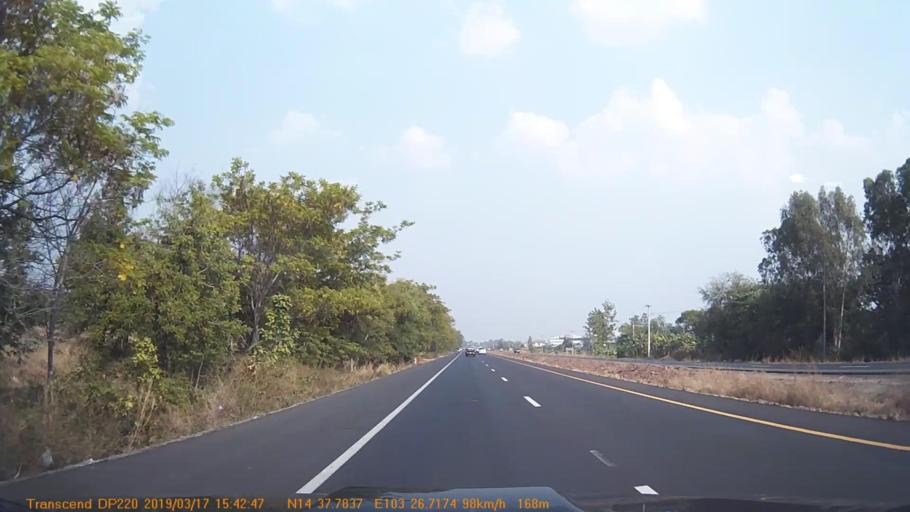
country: TH
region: Surin
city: Prasat
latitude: 14.6296
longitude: 103.4456
